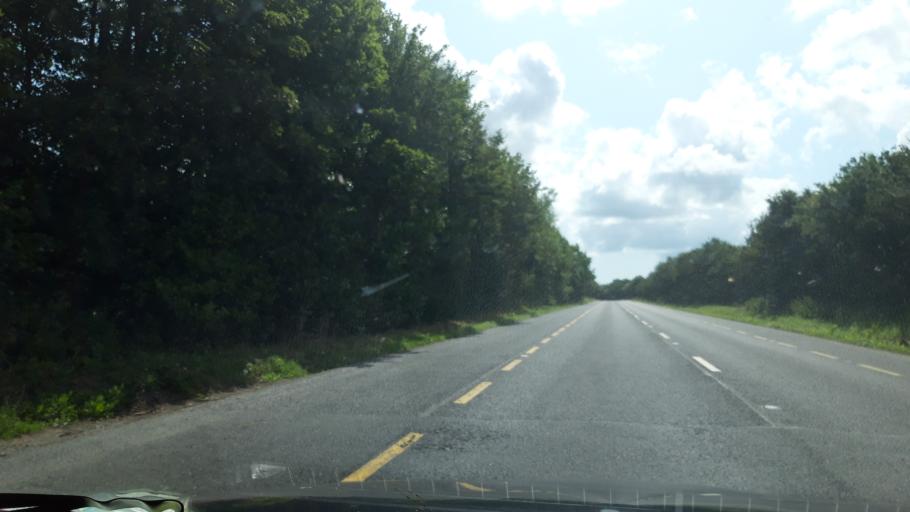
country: IE
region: Munster
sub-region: Waterford
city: Waterford
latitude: 52.2789
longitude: -7.0578
